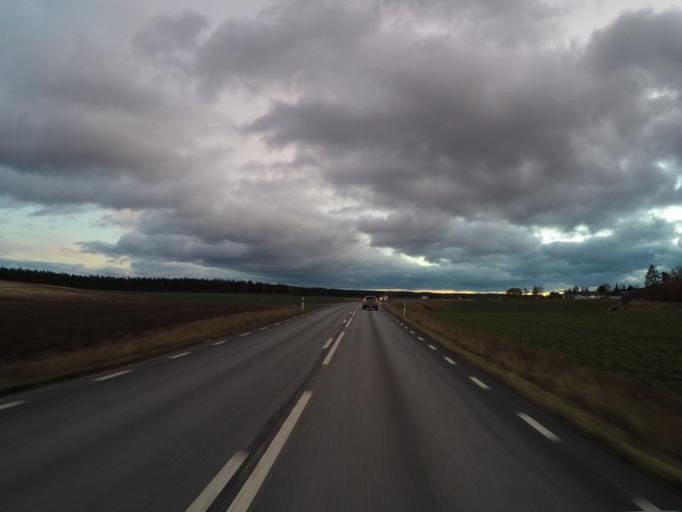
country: SE
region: Skane
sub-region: Kristianstads Kommun
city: Degeberga
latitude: 55.8459
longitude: 14.0962
